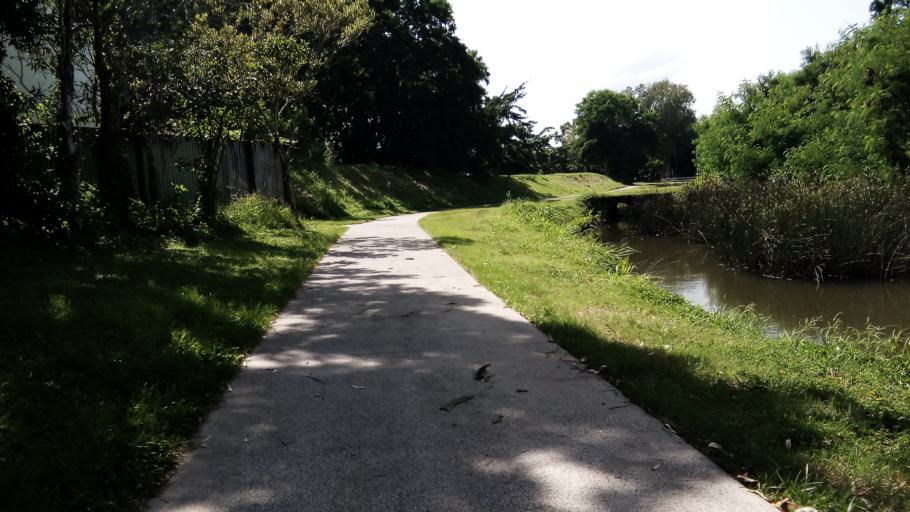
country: AU
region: Queensland
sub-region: Cairns
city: Cairns
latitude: -16.9127
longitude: 145.7603
